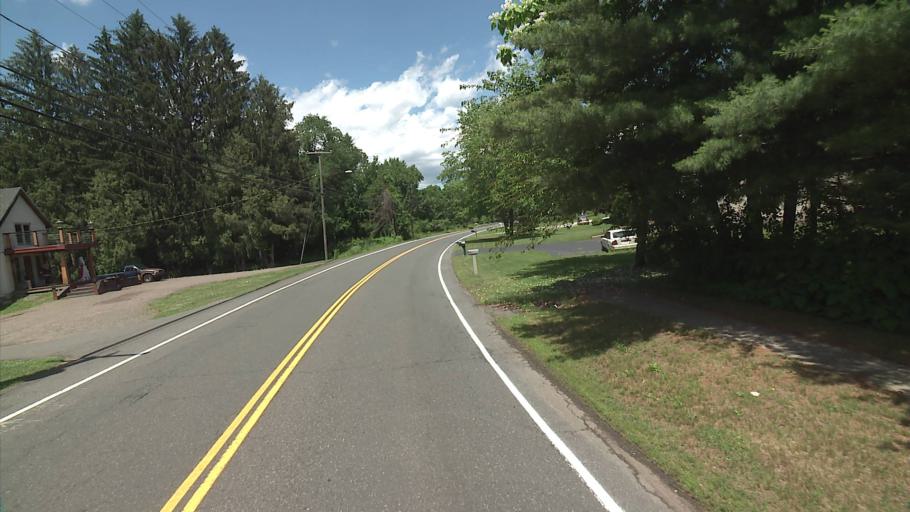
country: US
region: Connecticut
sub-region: Hartford County
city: Sherwood Manor
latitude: 42.0147
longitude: -72.5422
